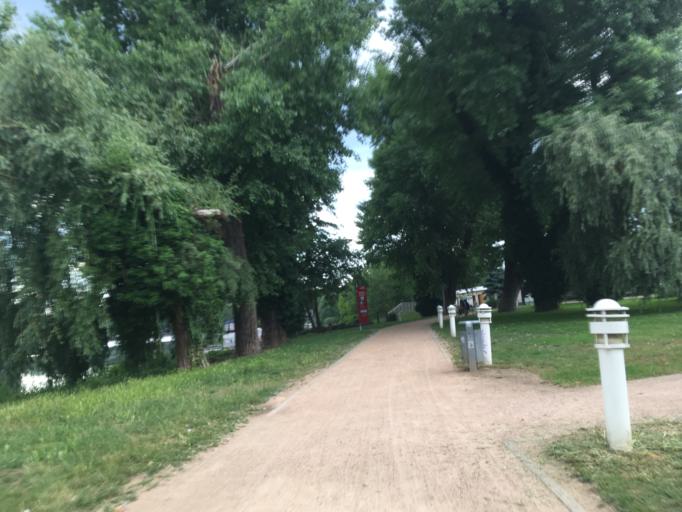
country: DE
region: Brandenburg
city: Furstenwalde
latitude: 52.3601
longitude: 14.0548
